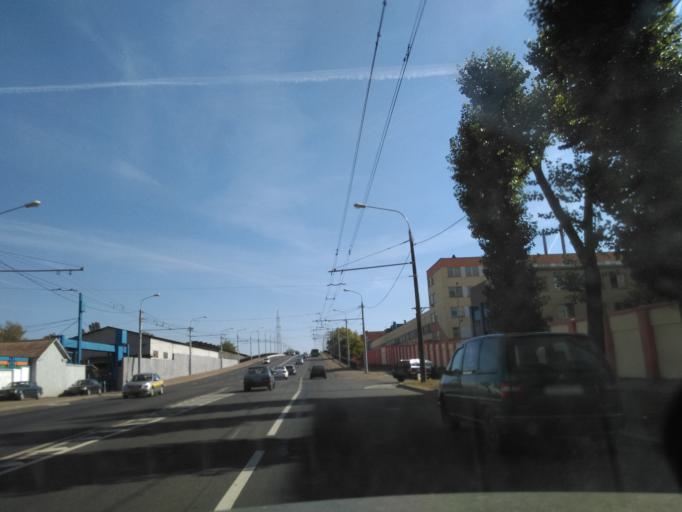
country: BY
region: Minsk
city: Minsk
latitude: 53.8899
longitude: 27.6335
